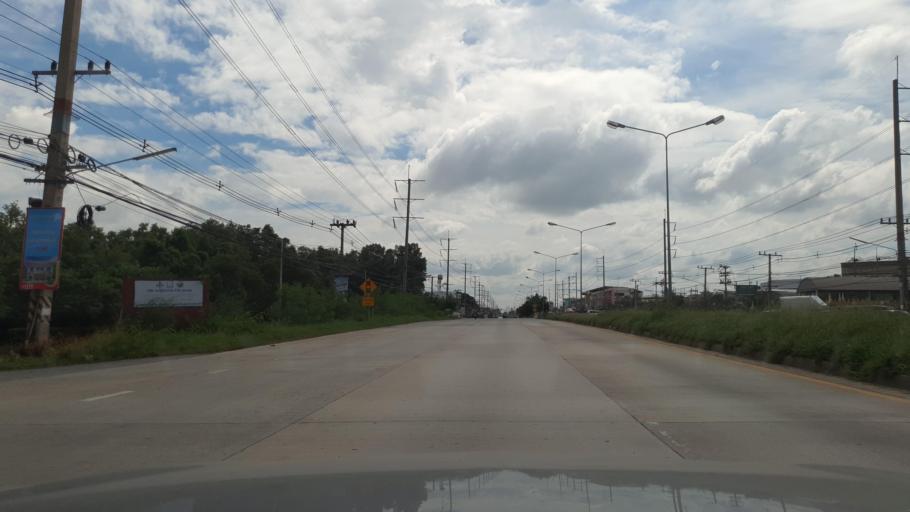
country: TH
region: Chachoengsao
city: Bang Pakong
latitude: 13.5507
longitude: 100.9905
